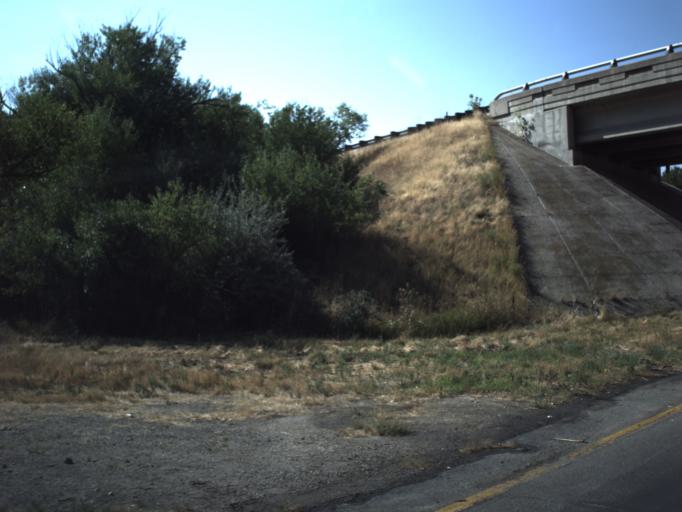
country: US
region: Utah
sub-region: Davis County
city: Farmington
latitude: 40.9734
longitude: -111.8925
